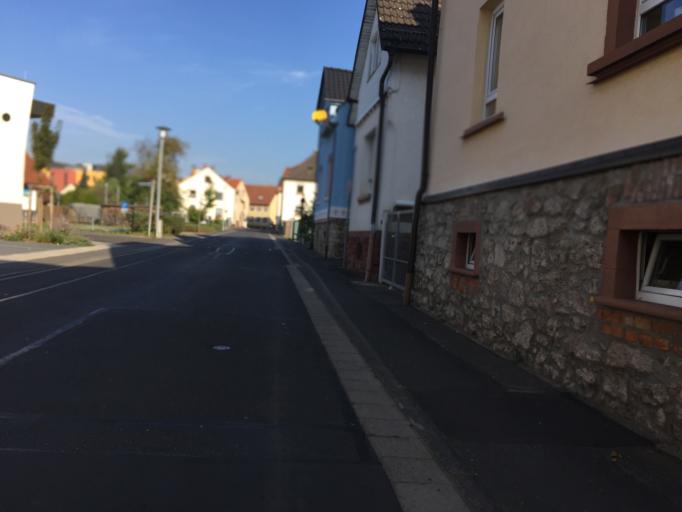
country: DE
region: Bavaria
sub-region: Regierungsbezirk Unterfranken
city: Goldbach
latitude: 49.9963
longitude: 9.1857
